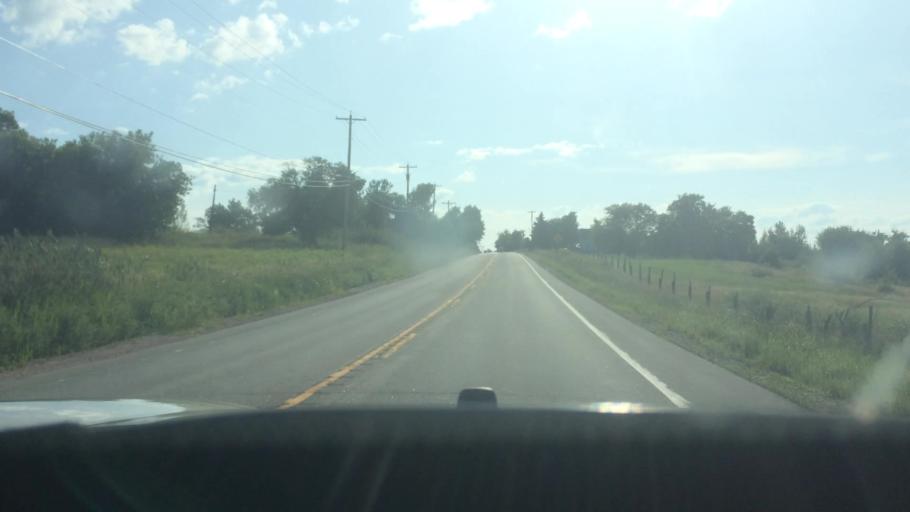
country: US
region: New York
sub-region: Franklin County
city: Malone
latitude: 44.7992
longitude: -74.4526
